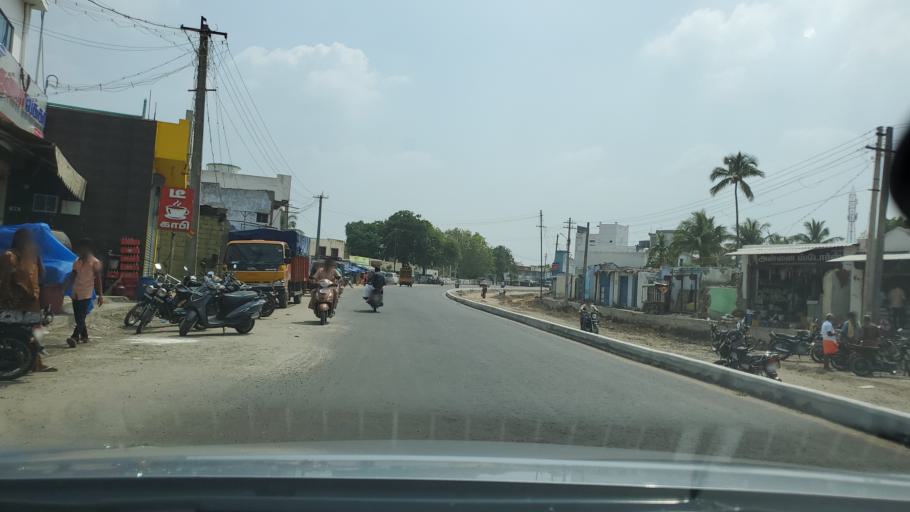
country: IN
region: Tamil Nadu
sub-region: Tiruppur
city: Kangayam
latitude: 10.9432
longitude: 77.4371
